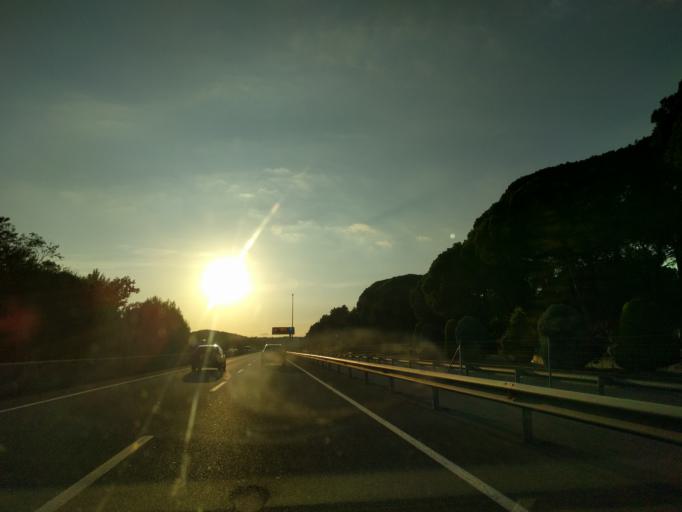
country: ES
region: Catalonia
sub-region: Provincia de Girona
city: Santa Cristina d'Aro
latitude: 41.8272
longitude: 2.9542
